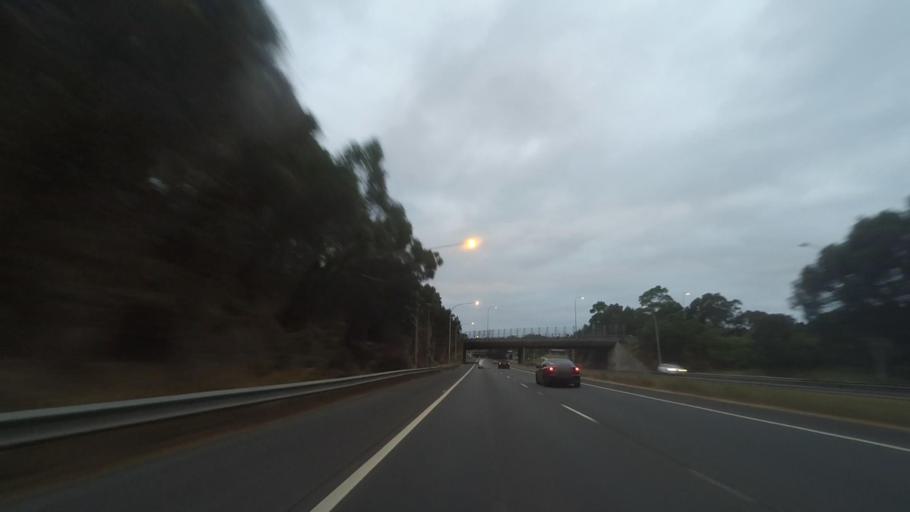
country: AU
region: New South Wales
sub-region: Wollongong
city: Mount Saint Thomas
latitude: -34.4420
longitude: 150.8634
